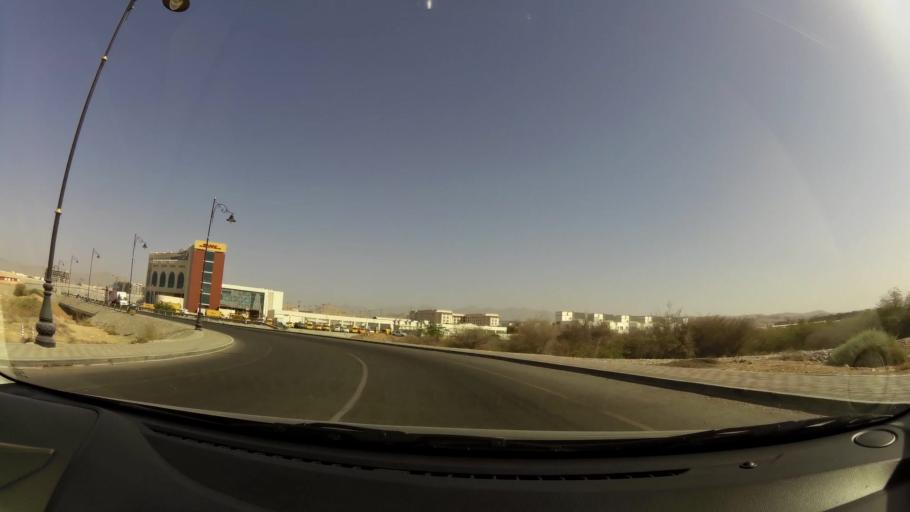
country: OM
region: Muhafazat Masqat
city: Bawshar
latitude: 23.5819
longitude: 58.2915
